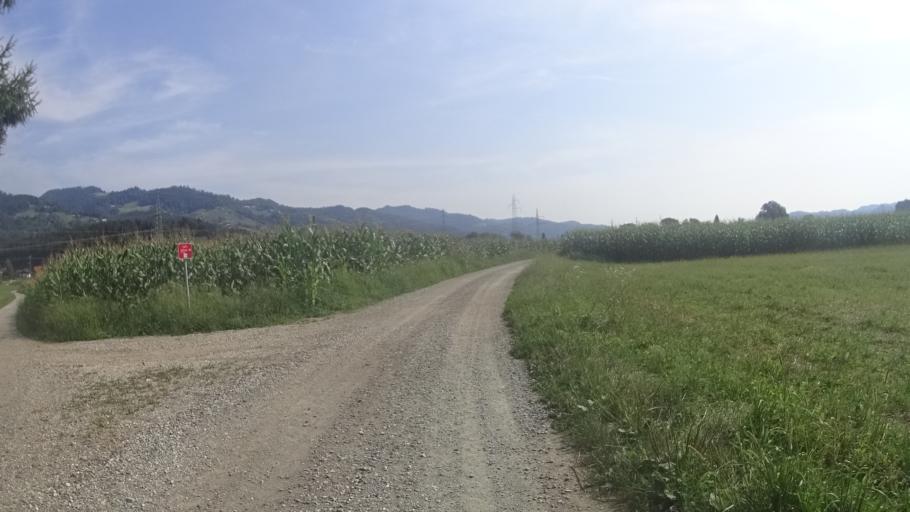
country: SI
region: Selnica ob Dravi
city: Selnica ob Dravi
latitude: 46.5440
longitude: 15.4779
